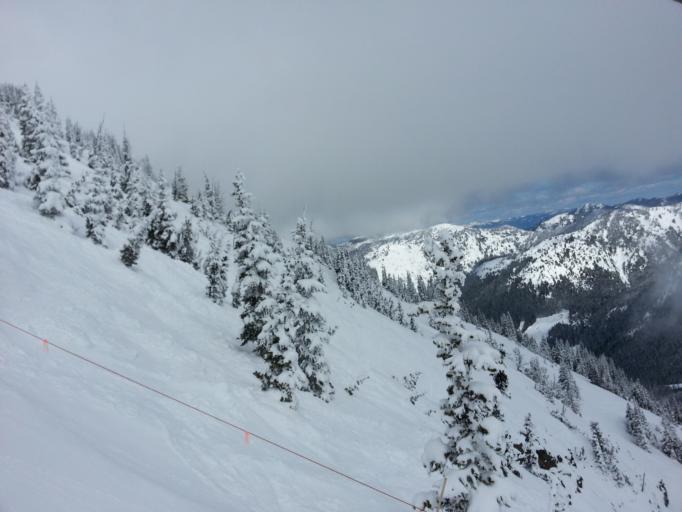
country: US
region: Washington
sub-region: King County
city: Enumclaw
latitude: 46.9270
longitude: -121.5041
